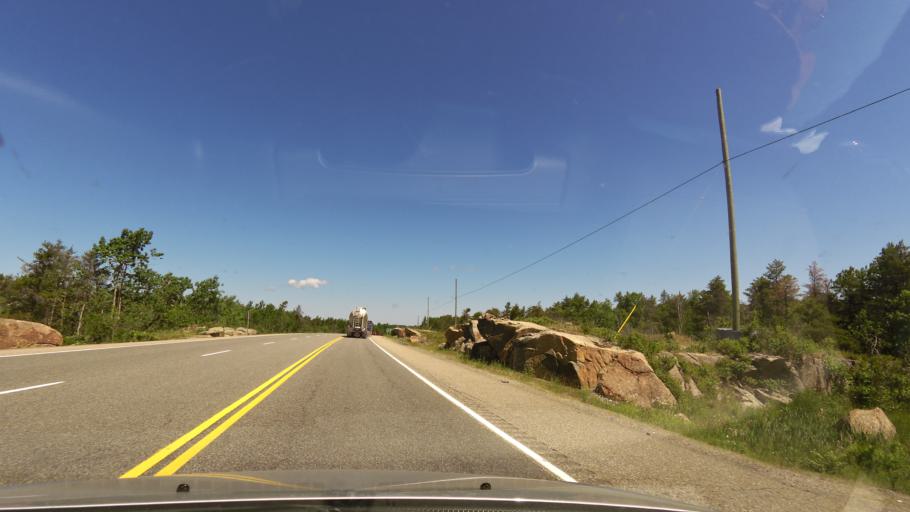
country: CA
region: Ontario
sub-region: Parry Sound District
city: Parry Sound
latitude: 45.7647
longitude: -80.4954
